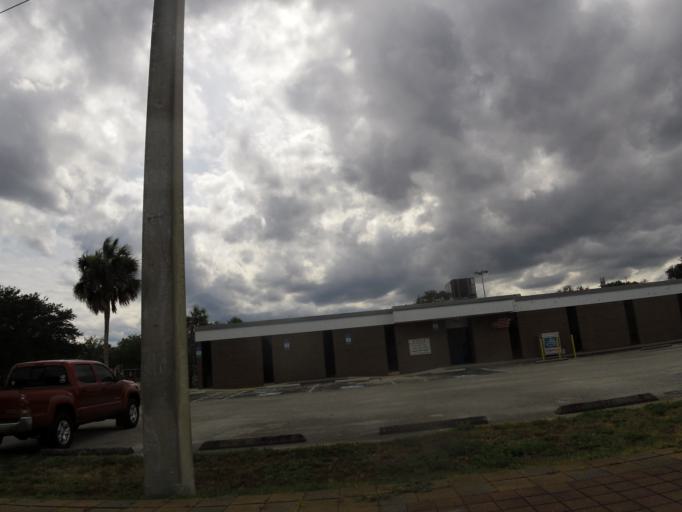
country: US
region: Florida
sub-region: Duval County
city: Jacksonville Beach
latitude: 30.2864
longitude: -81.4046
